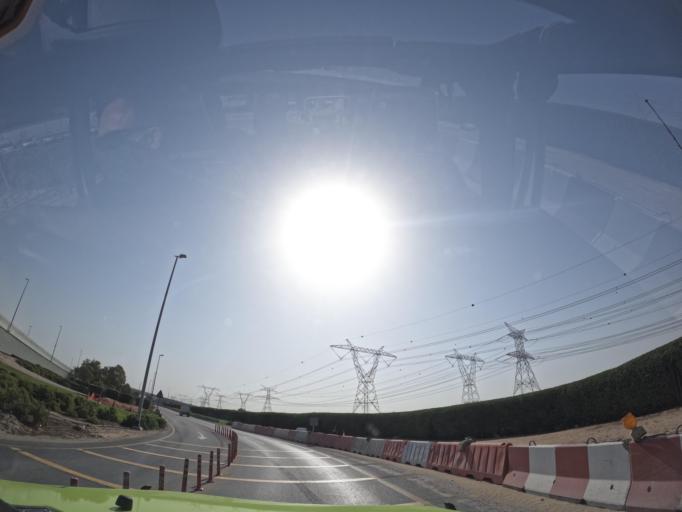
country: AE
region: Dubai
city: Dubai
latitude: 25.1702
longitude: 55.3150
